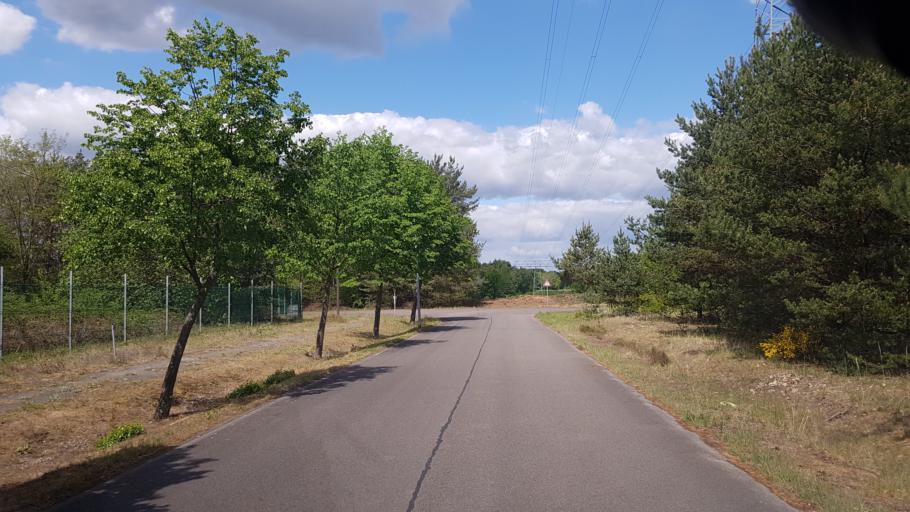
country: DE
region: Brandenburg
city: Altdobern
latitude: 51.6483
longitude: 14.0031
